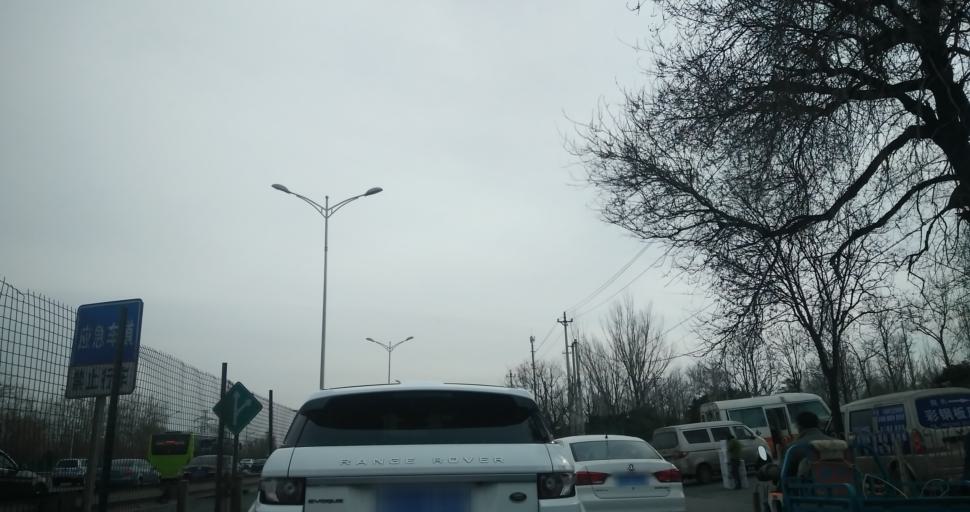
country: CN
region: Beijing
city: Huaxiang
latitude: 39.8354
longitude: 116.3394
